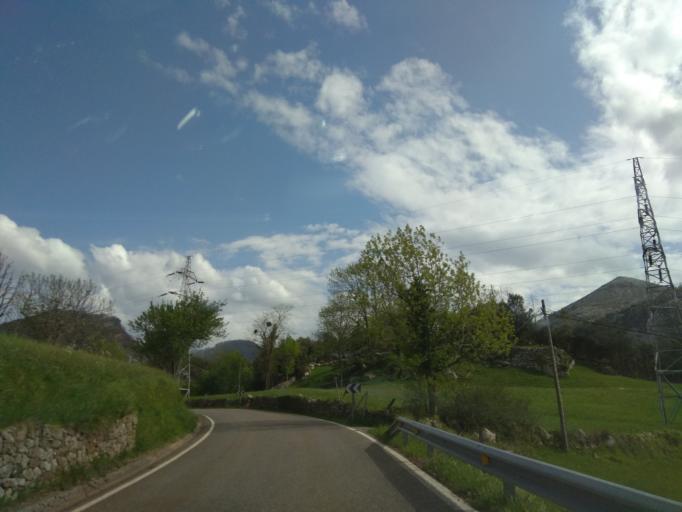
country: ES
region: Cantabria
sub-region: Provincia de Cantabria
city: Tresviso
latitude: 43.2515
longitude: -4.5894
